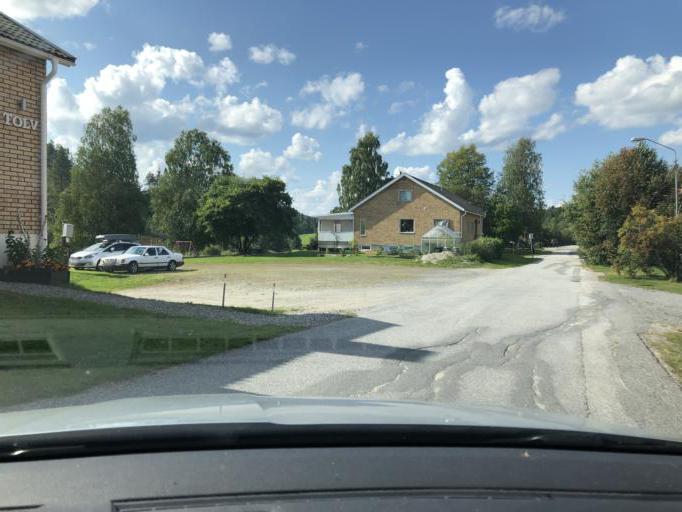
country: SE
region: Vaesternorrland
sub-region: OErnskoeldsviks Kommun
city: Bredbyn
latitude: 63.4469
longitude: 18.1090
